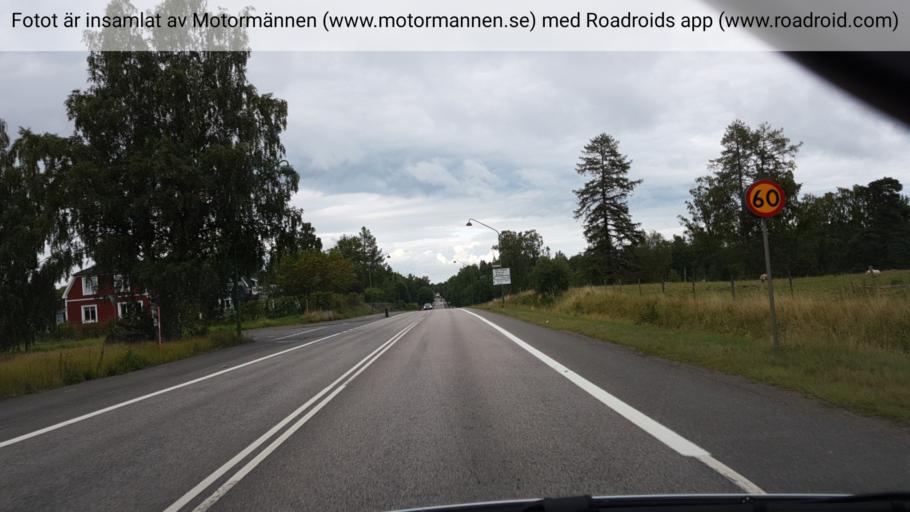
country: SE
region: Vaestra Goetaland
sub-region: Tidaholms Kommun
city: Tidaholm
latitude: 58.1655
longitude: 13.9400
